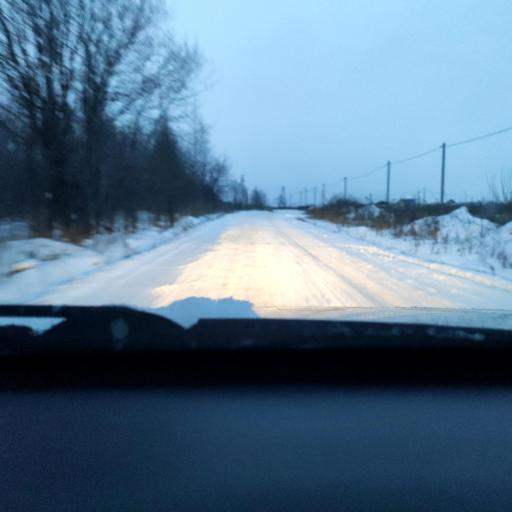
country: RU
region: Perm
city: Froly
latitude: 57.9475
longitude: 56.2304
